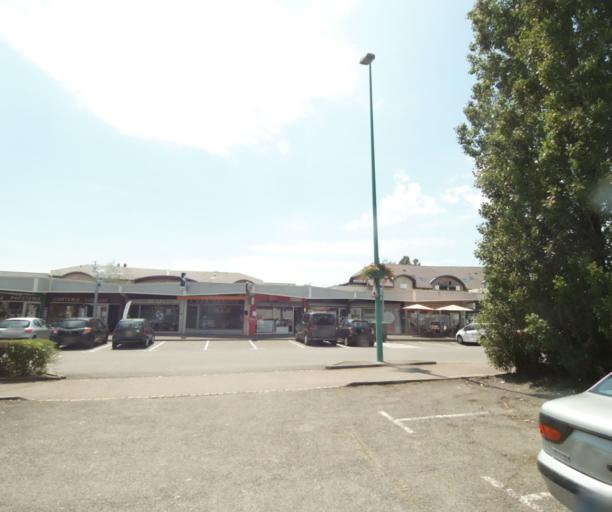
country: FR
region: Rhone-Alpes
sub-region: Departement de la Haute-Savoie
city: Douvaine
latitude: 46.3068
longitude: 6.3102
